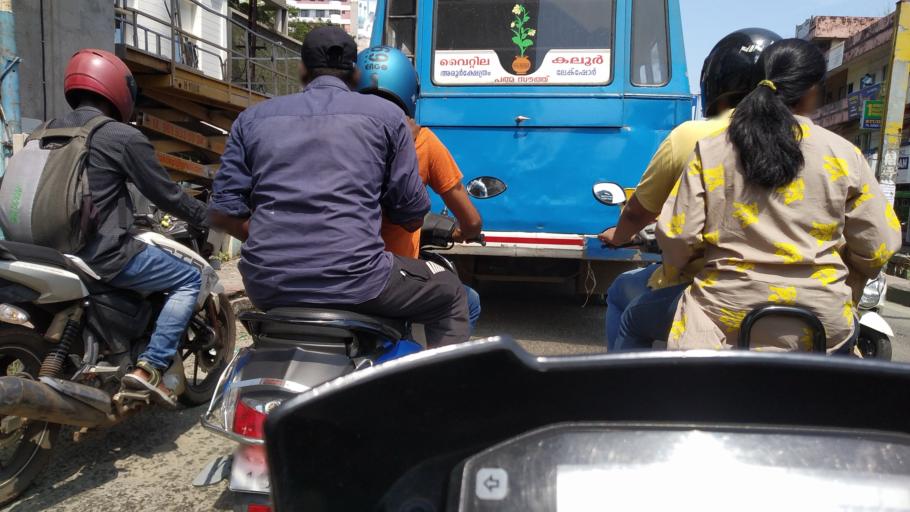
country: IN
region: Kerala
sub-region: Ernakulam
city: Cochin
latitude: 9.9655
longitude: 76.2936
